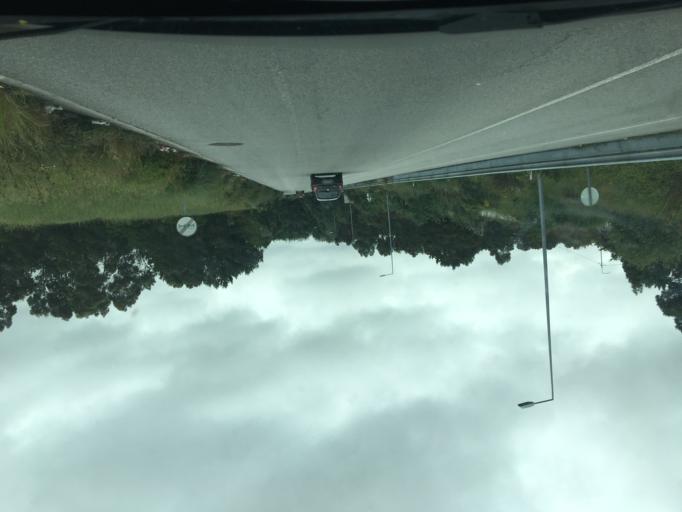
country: PT
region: Porto
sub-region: Matosinhos
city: Santa Cruz do Bispo
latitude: 41.2221
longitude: -8.6707
